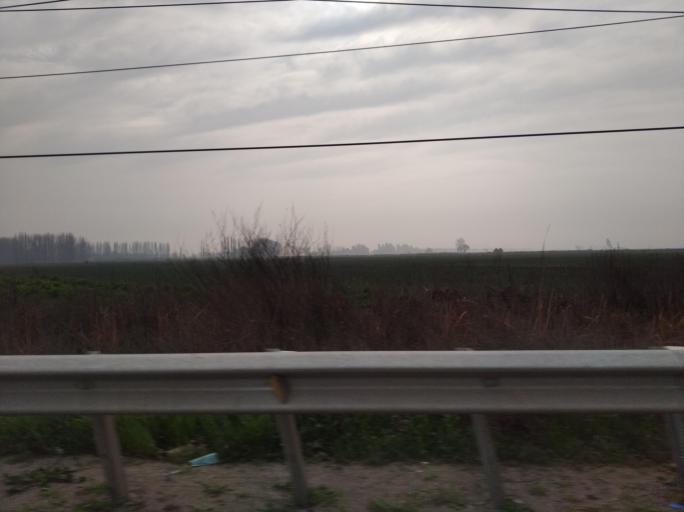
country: CL
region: Santiago Metropolitan
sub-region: Provincia de Chacabuco
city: Lampa
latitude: -33.3235
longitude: -70.8269
